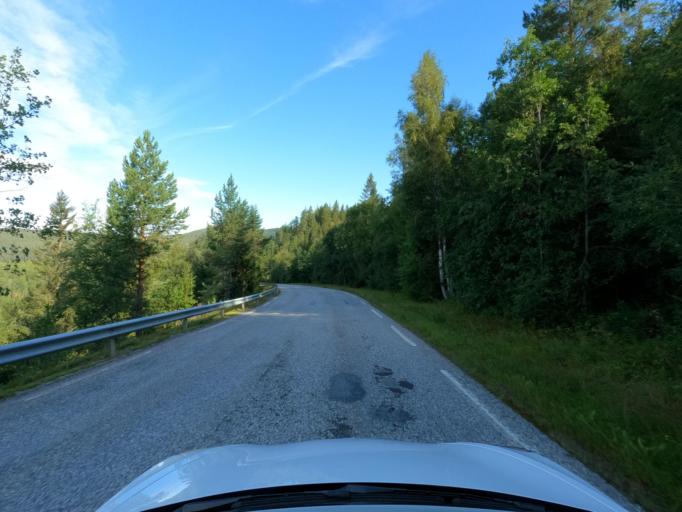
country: NO
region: Telemark
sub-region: Hjartdal
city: Sauland
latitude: 59.9185
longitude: 8.9799
